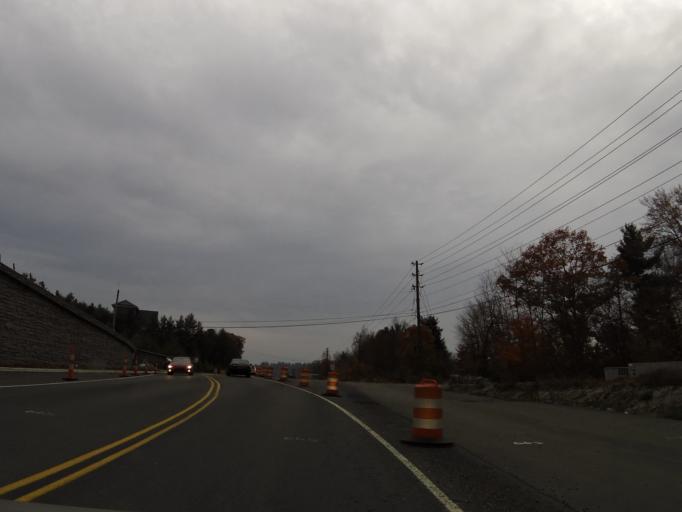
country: US
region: North Carolina
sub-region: Watauga County
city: Blowing Rock
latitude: 36.1373
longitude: -81.6705
